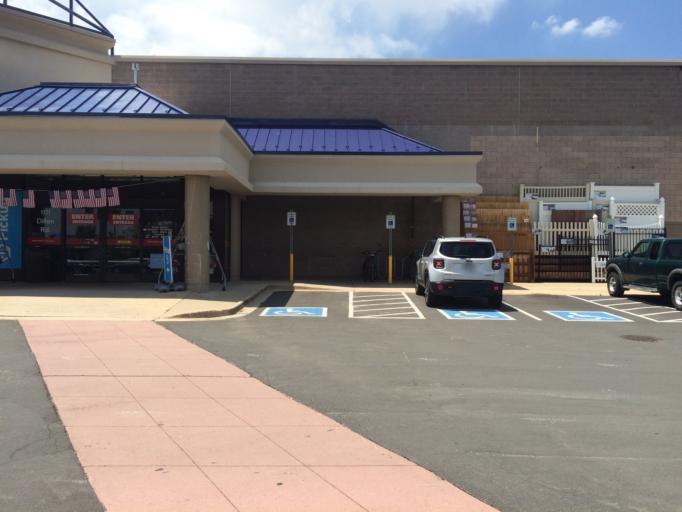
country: US
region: Colorado
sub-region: Boulder County
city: Superior
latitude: 39.9635
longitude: -105.1663
